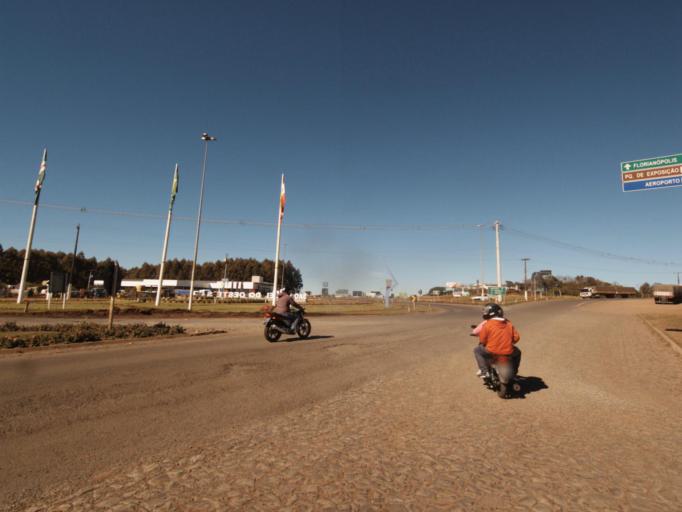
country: AR
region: Misiones
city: Bernardo de Irigoyen
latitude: -26.7611
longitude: -53.5009
